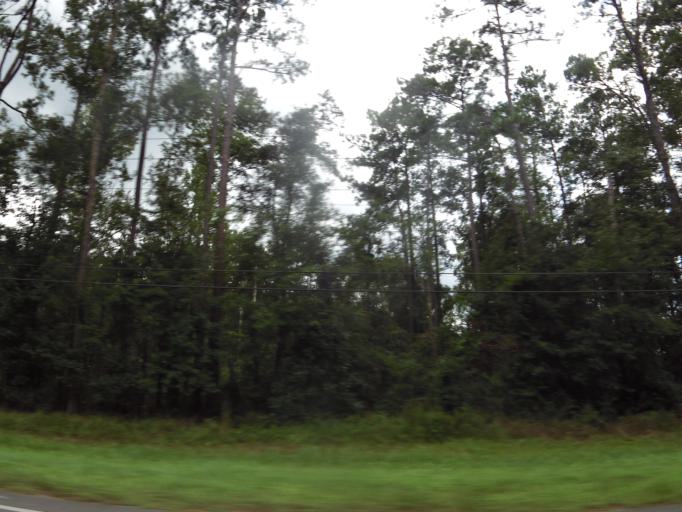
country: US
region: Florida
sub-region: Clay County
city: Middleburg
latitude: 30.0586
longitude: -81.8695
